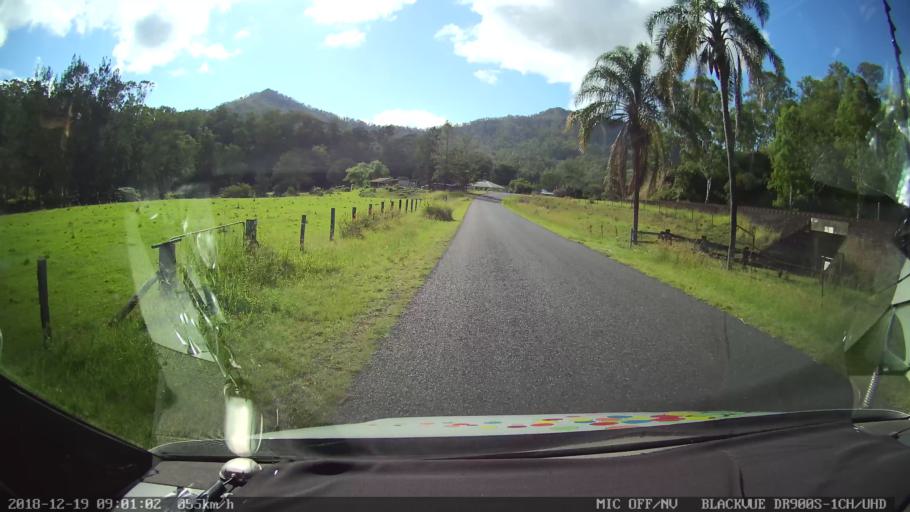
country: AU
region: New South Wales
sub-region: Kyogle
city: Kyogle
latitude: -28.4361
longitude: 152.9581
